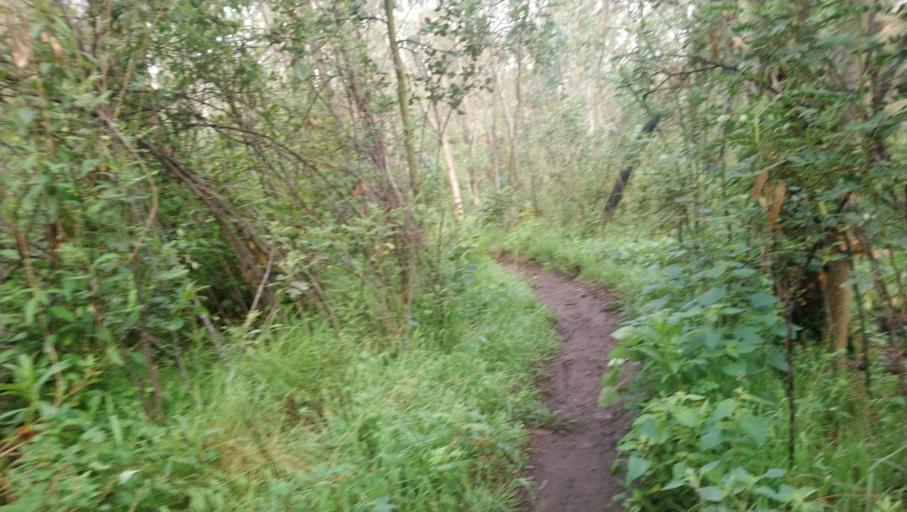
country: MX
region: Mexico
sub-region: Tultitlan
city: Ampliacion San Mateo (Colonia Solidaridad)
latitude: 19.6064
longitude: -99.1222
